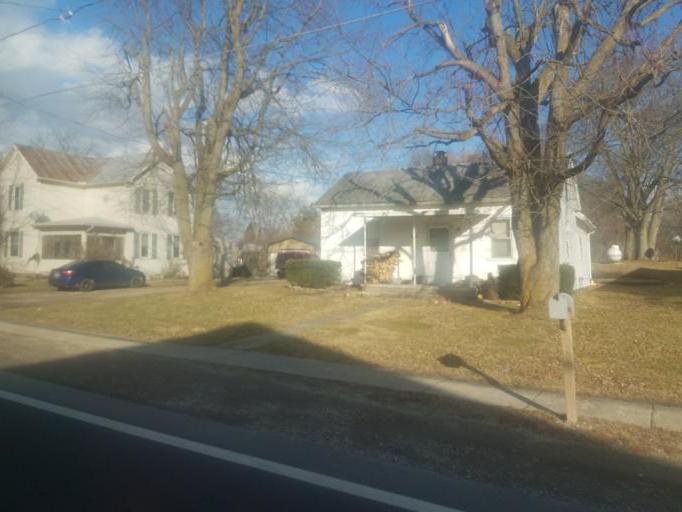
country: US
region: Ohio
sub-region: Marion County
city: Prospect
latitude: 40.3829
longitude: -83.1502
